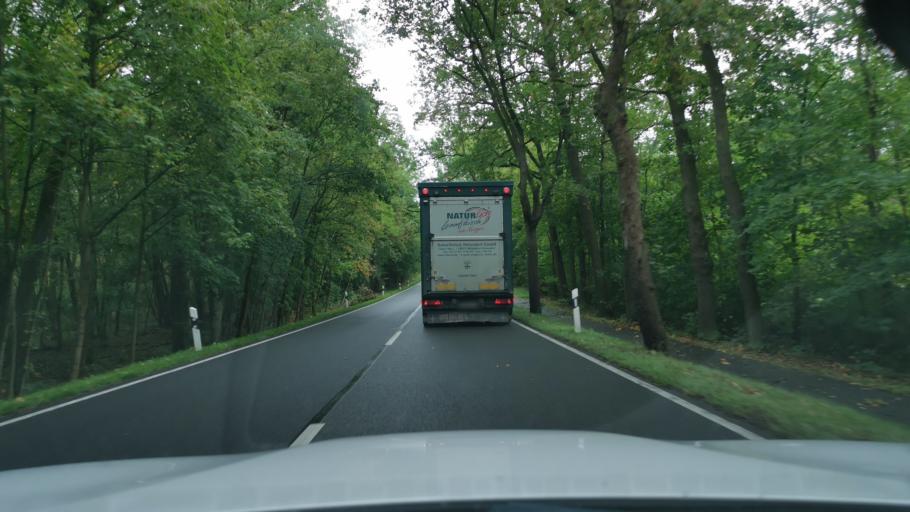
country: DE
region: Brandenburg
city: Treuenbrietzen
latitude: 52.0758
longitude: 12.8849
